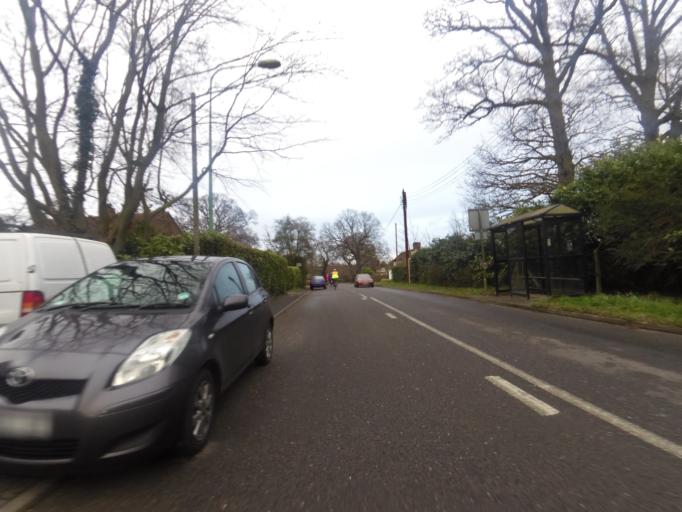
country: GB
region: England
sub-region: Suffolk
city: Ipswich
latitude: 52.0814
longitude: 1.1660
